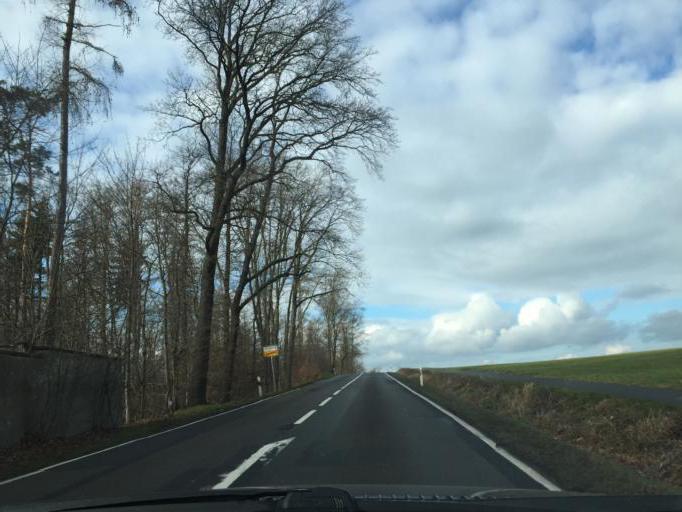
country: DE
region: Saxony
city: Wachau
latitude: 51.1422
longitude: 13.9114
